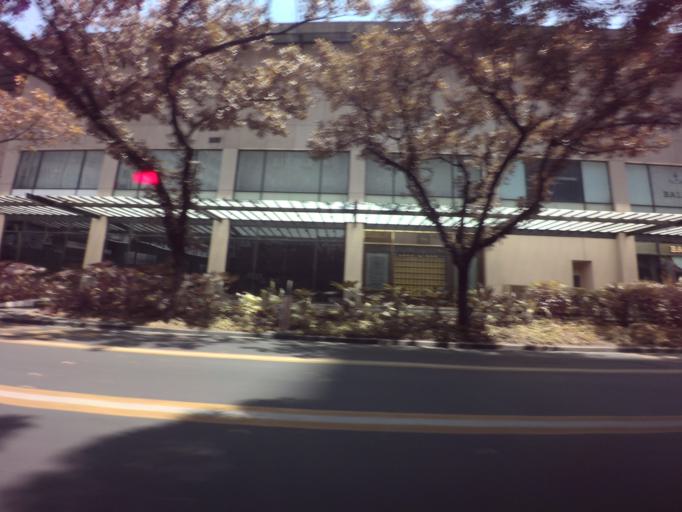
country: PH
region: Metro Manila
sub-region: Makati City
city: Makati City
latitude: 14.5537
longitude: 121.0224
